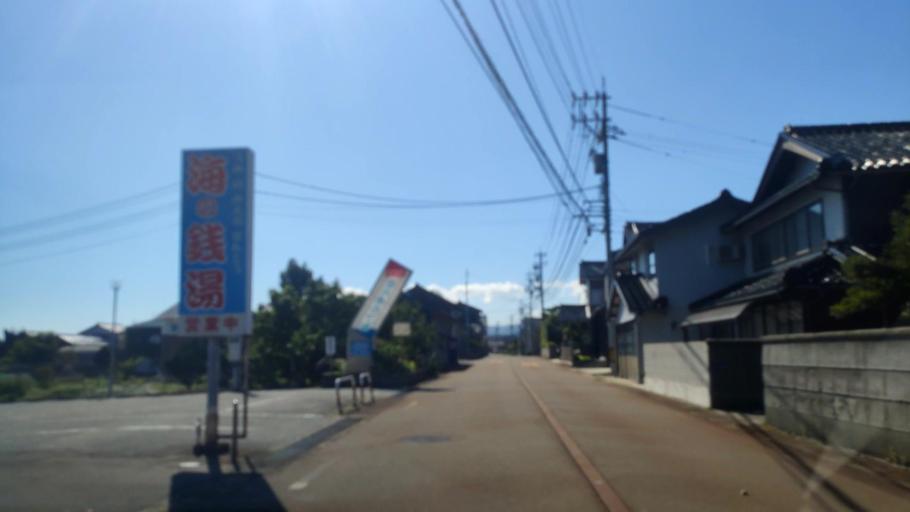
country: JP
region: Ishikawa
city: Nanao
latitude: 37.4402
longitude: 137.2734
